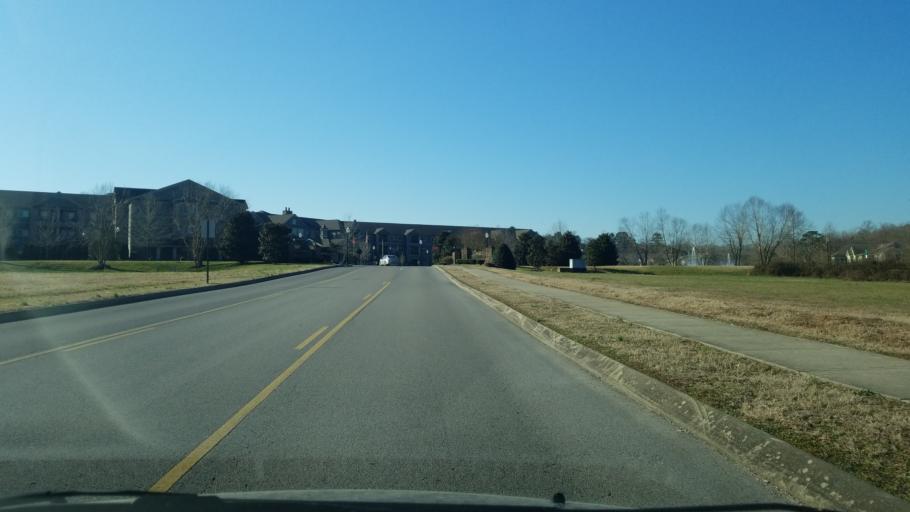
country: US
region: Tennessee
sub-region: Hamilton County
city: Collegedale
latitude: 35.0567
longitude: -85.0725
